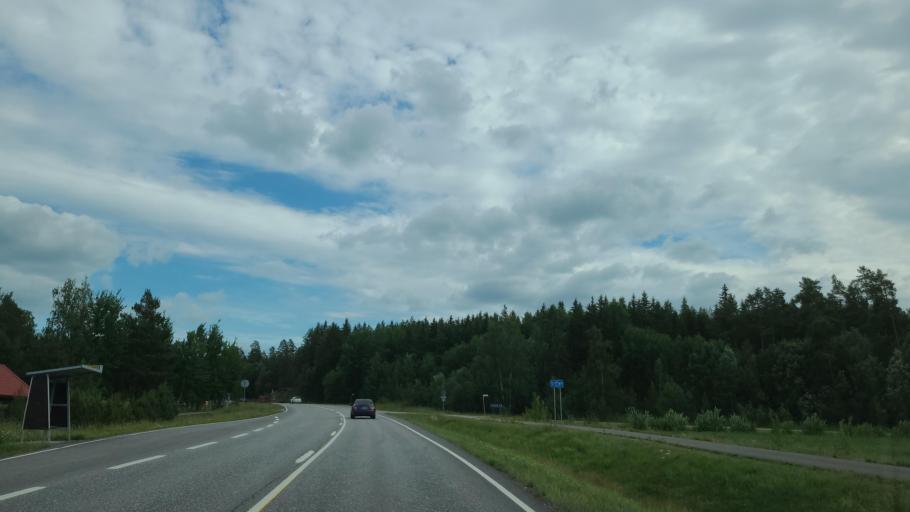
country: FI
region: Varsinais-Suomi
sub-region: Turku
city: Rymaettylae
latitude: 60.3922
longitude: 21.9059
